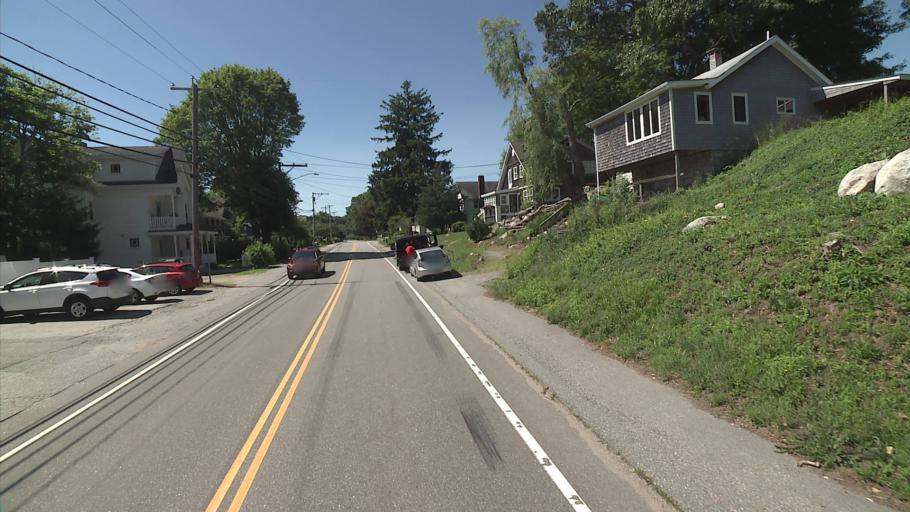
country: US
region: Connecticut
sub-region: New London County
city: Noank
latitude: 41.3362
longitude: -71.9923
